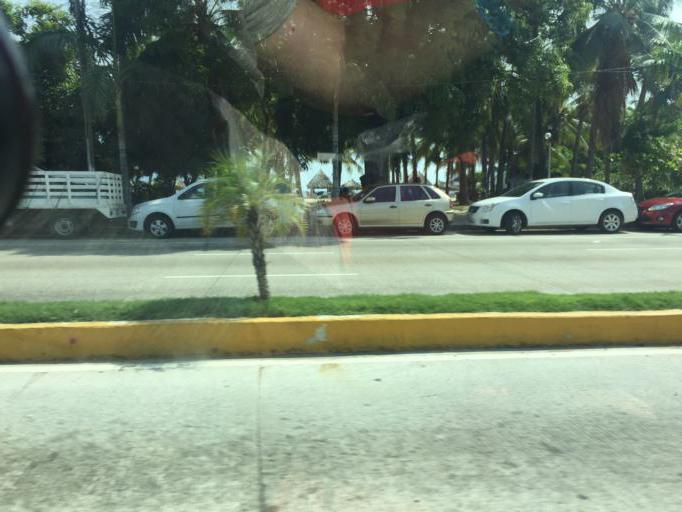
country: MX
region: Guerrero
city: Acapulco de Juarez
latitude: 16.8569
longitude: -99.8939
